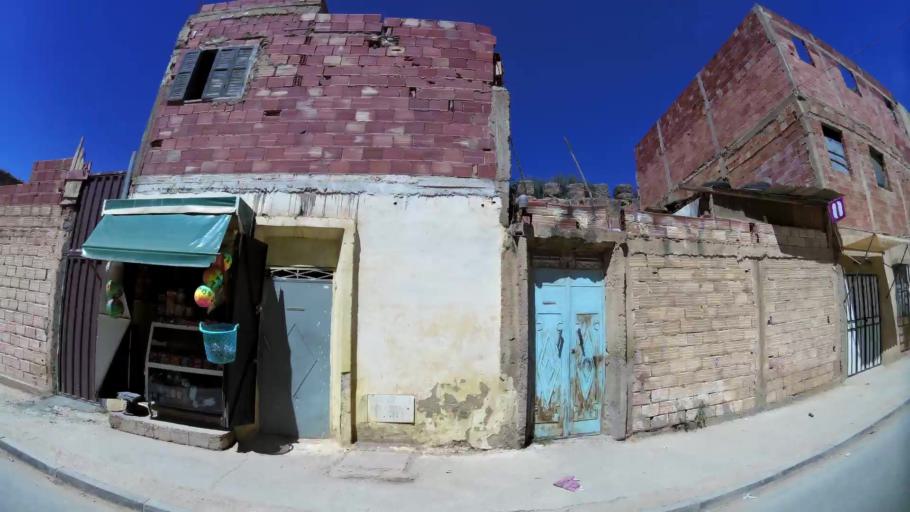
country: MA
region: Meknes-Tafilalet
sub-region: Meknes
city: Meknes
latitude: 33.8674
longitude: -5.5604
